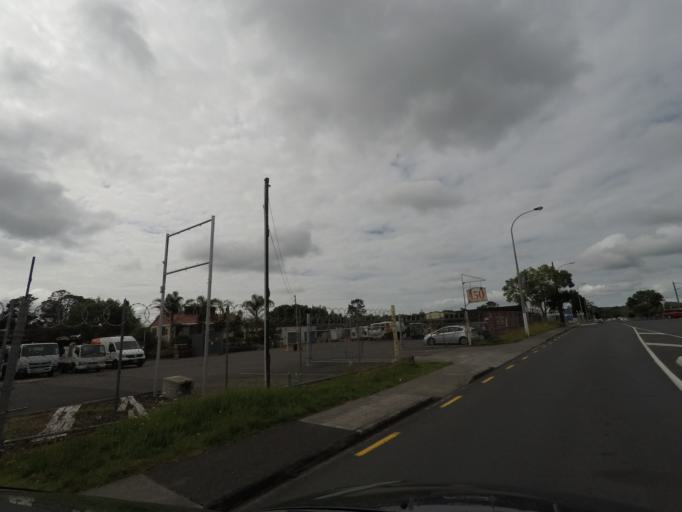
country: NZ
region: Auckland
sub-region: Auckland
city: Waitakere
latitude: -36.8902
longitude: 174.6318
